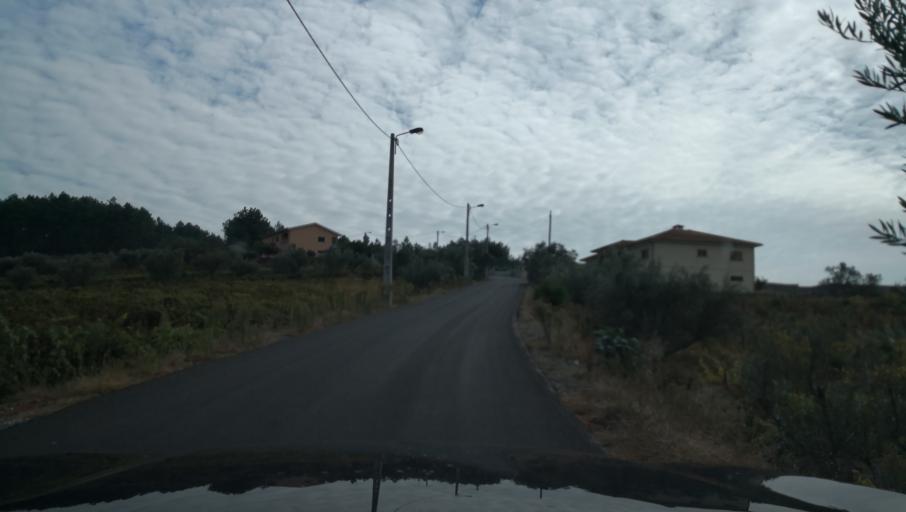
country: PT
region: Vila Real
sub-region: Sabrosa
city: Vilela
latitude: 41.2117
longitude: -7.6861
